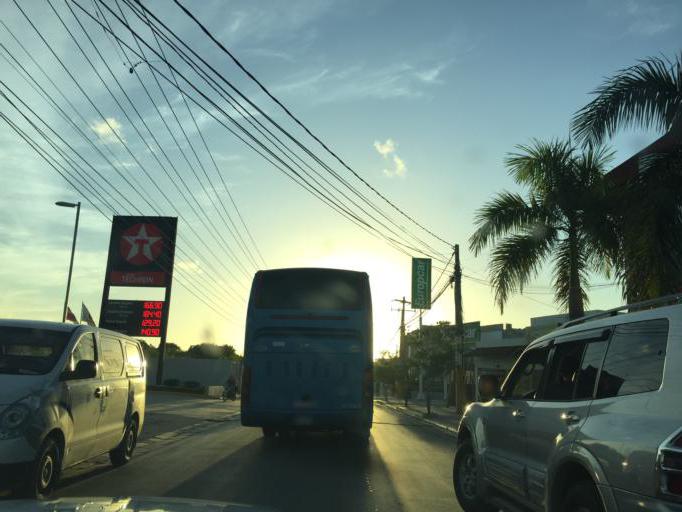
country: DO
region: San Juan
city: Punta Cana
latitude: 18.6910
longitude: -68.4385
